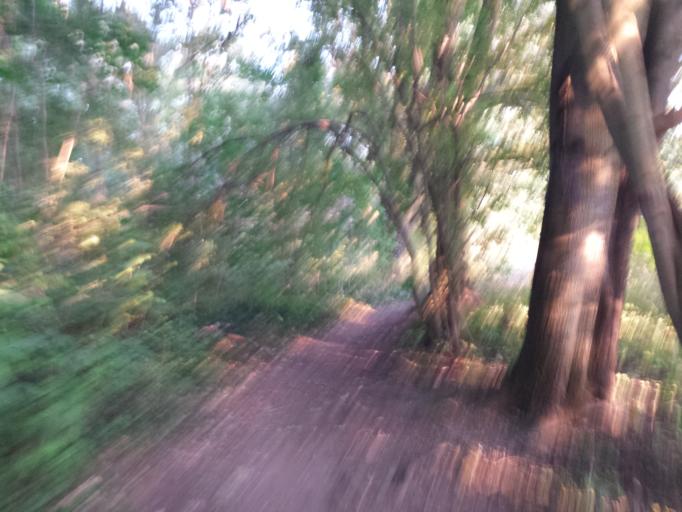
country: DE
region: Saxony
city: Markkleeberg
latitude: 51.2917
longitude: 12.3865
